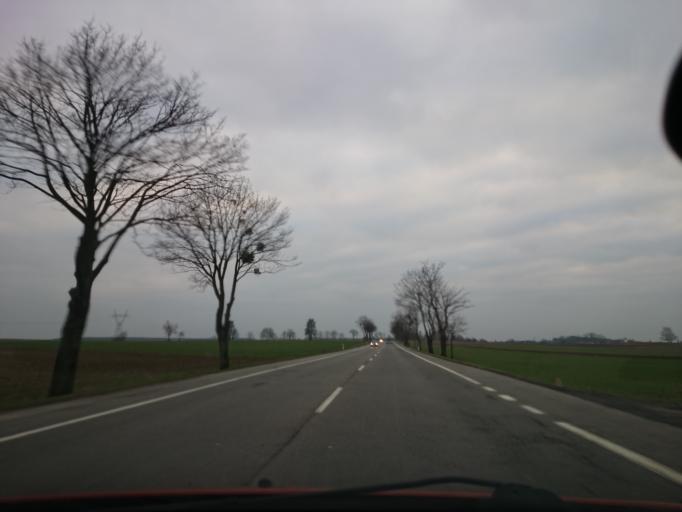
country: PL
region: Opole Voivodeship
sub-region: Powiat nyski
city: Lambinowice
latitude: 50.6027
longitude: 17.5443
